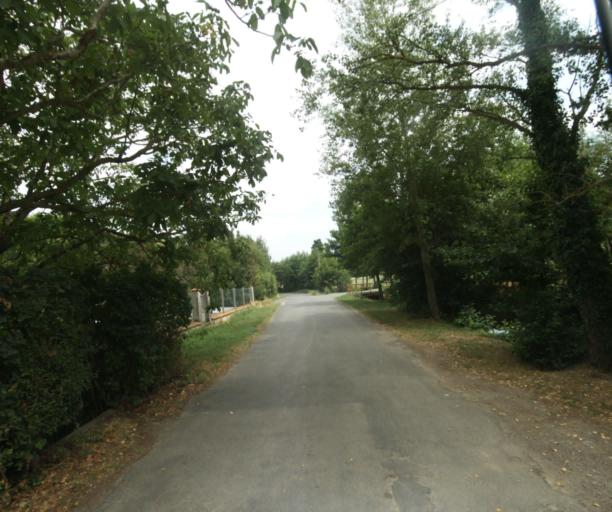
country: FR
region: Midi-Pyrenees
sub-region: Departement de la Haute-Garonne
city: Revel
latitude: 43.4535
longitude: 2.0171
